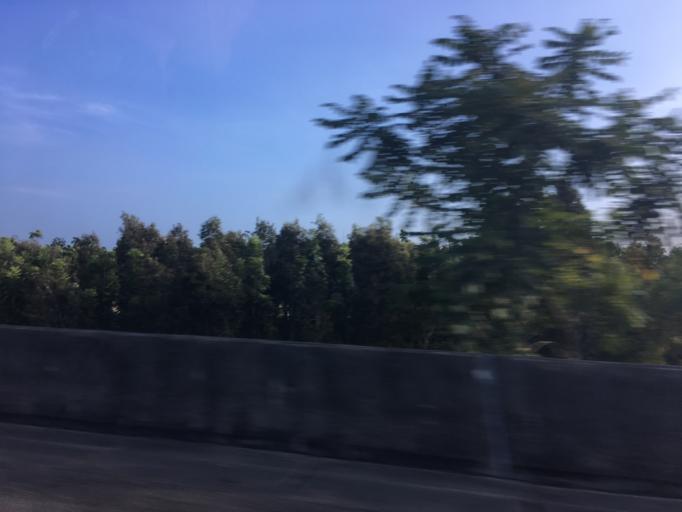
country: TW
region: Taiwan
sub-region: Chiayi
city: Taibao
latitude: 23.4275
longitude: 120.3420
